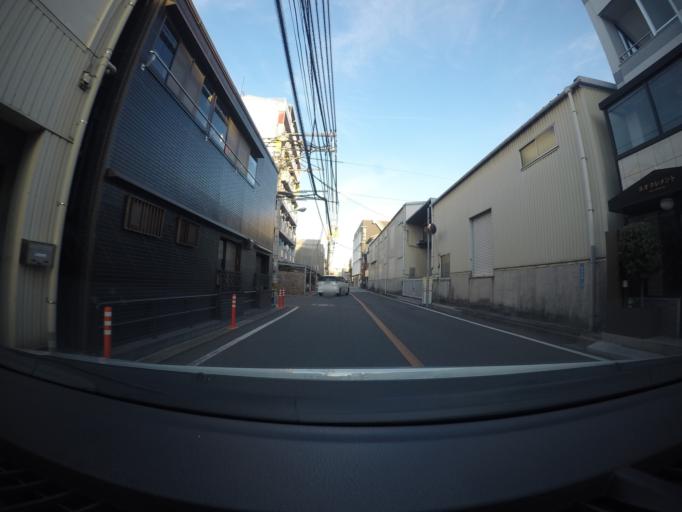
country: JP
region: Kochi
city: Kochi-shi
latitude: 33.5564
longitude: 133.5533
